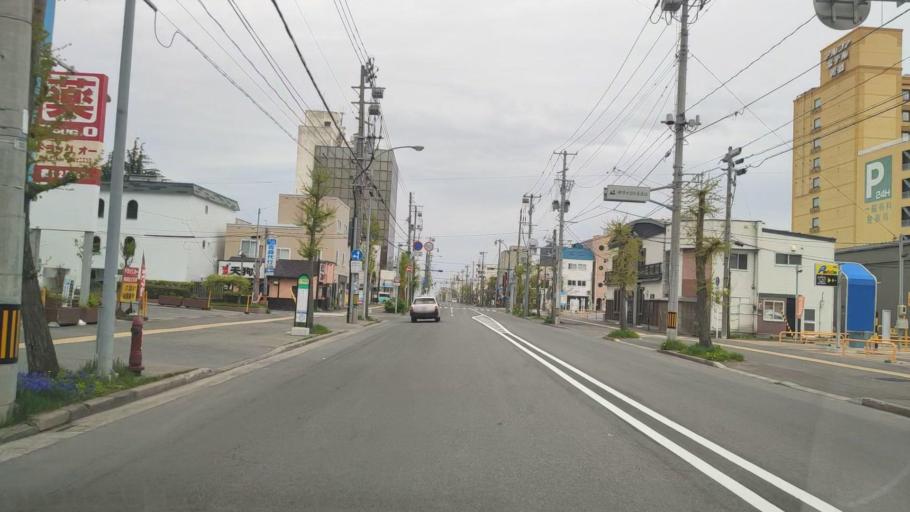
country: JP
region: Aomori
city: Aomori Shi
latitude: 40.8245
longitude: 140.7504
